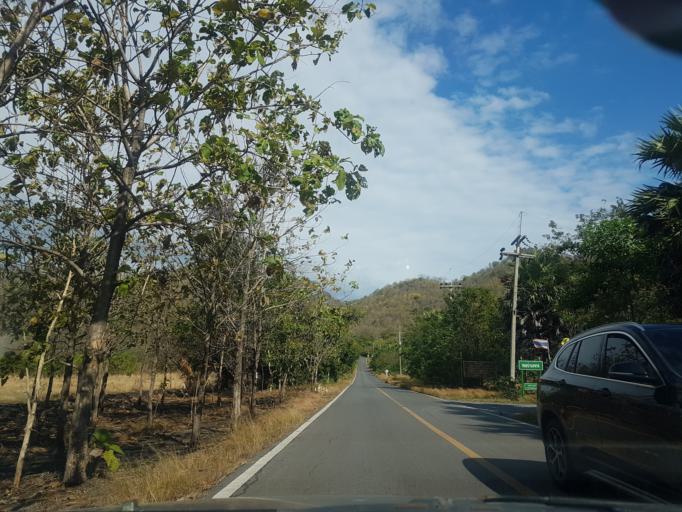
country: TH
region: Lop Buri
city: Lop Buri
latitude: 14.8192
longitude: 100.7509
